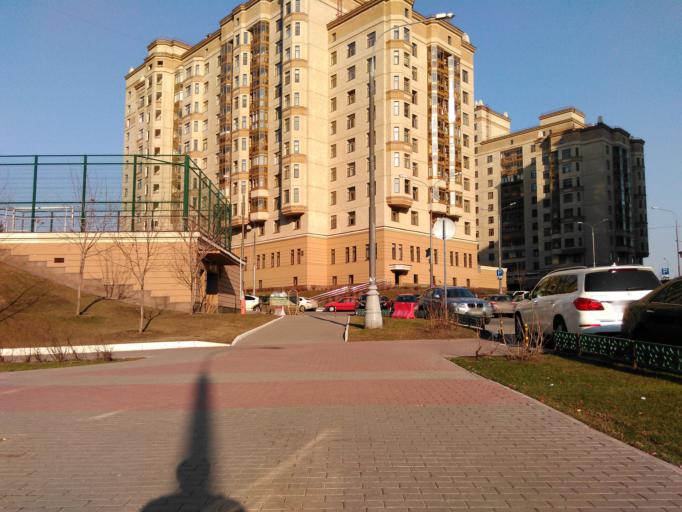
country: RU
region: Moscow
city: Ramenki
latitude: 55.7034
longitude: 37.5149
